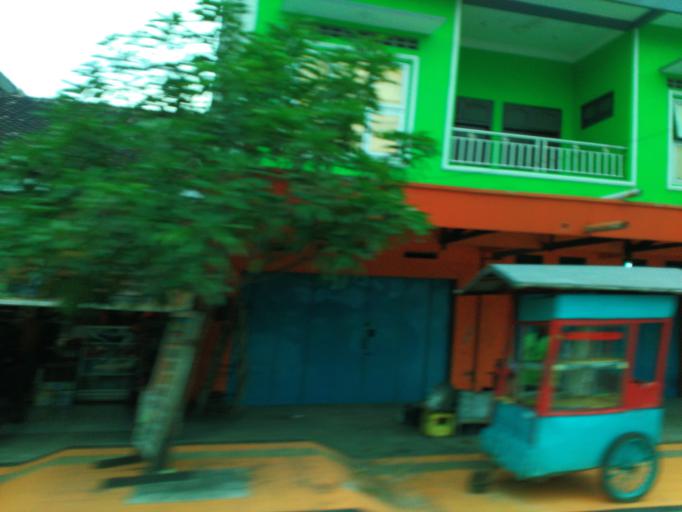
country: ID
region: Central Java
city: Gatak
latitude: -7.5944
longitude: 110.7029
